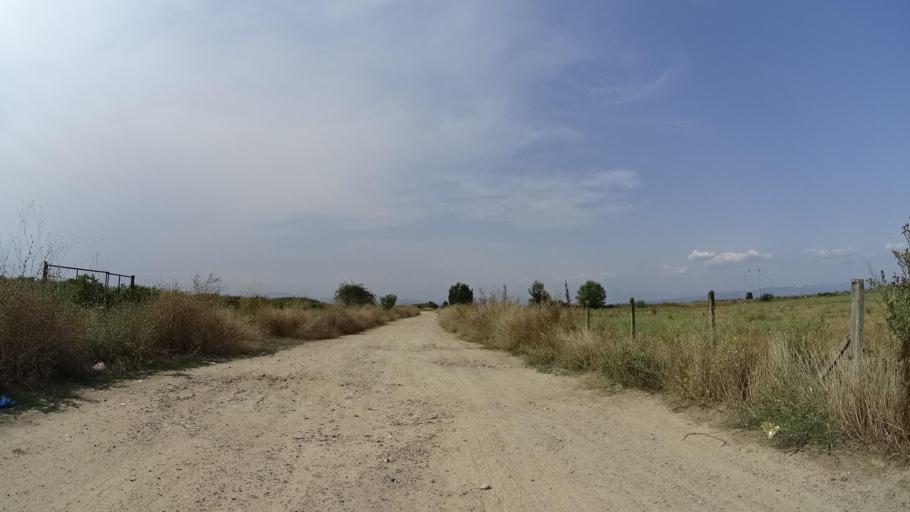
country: BG
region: Plovdiv
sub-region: Obshtina Kaloyanovo
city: Kaloyanovo
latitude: 42.2810
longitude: 24.7989
